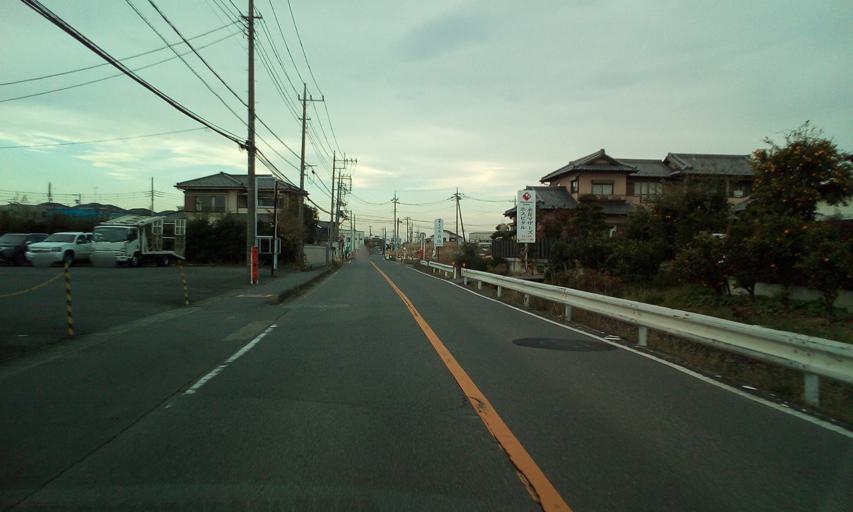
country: JP
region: Saitama
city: Yashio-shi
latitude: 35.8459
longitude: 139.8615
